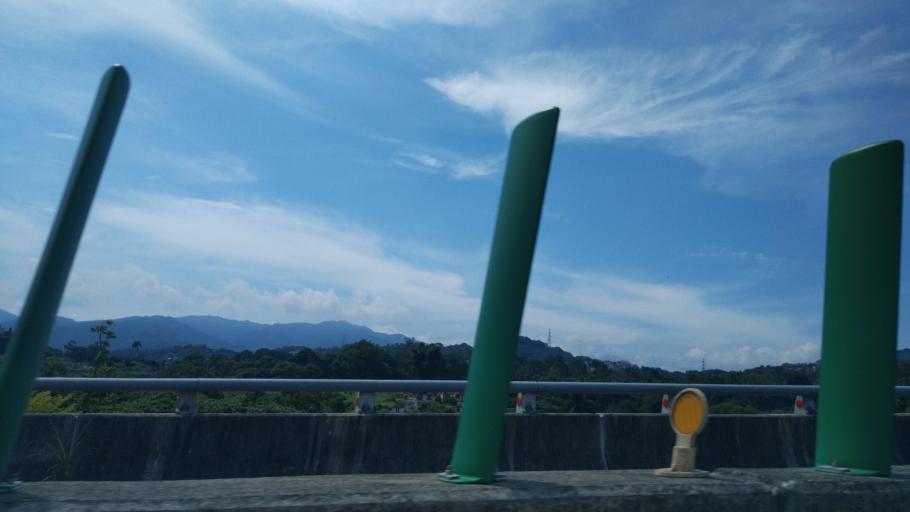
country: TW
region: Taipei
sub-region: Taipei
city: Banqiao
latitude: 24.9624
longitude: 121.5162
